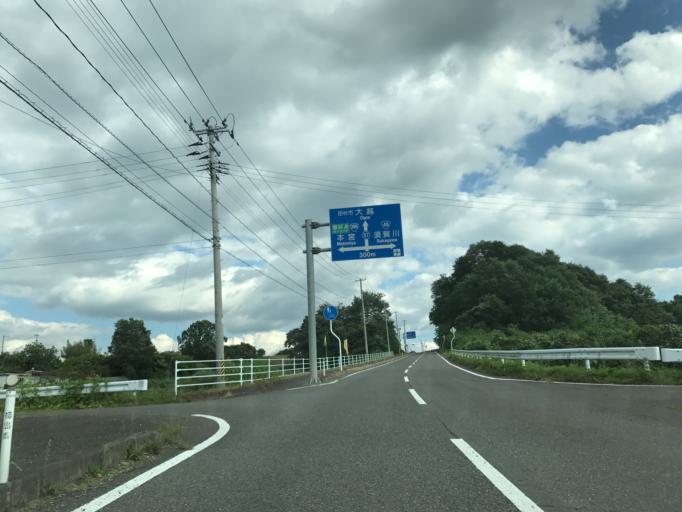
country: JP
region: Fukushima
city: Miharu
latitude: 37.4015
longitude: 140.4415
